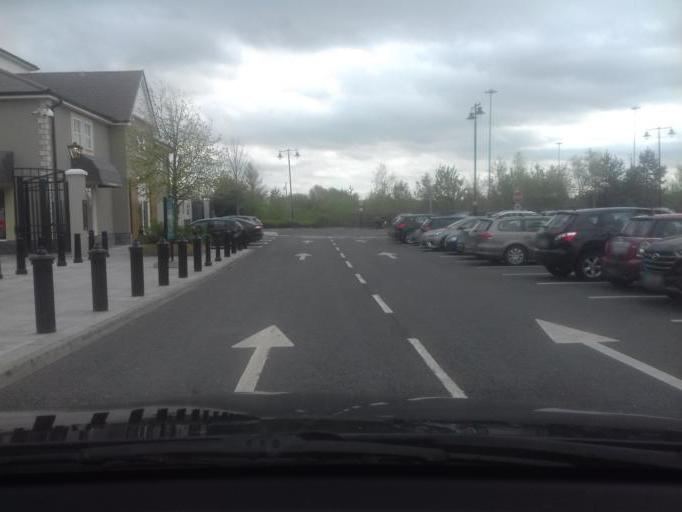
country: IE
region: Leinster
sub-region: Kildare
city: Kildare
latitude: 53.1532
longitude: -6.9175
